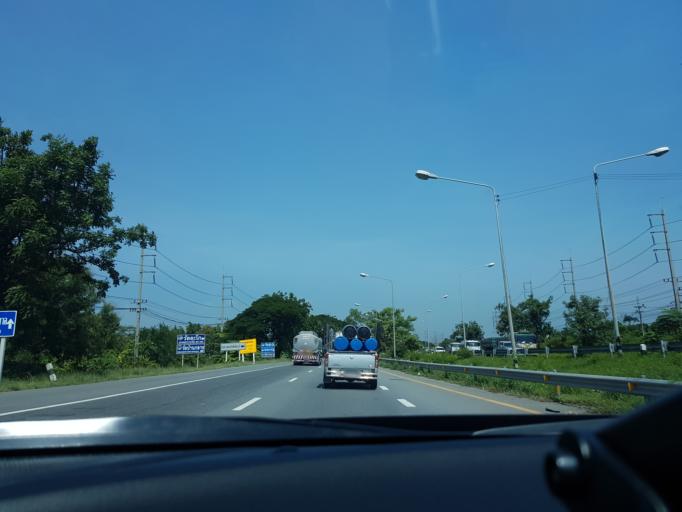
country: TH
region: Sara Buri
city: Saraburi
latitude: 14.5325
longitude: 100.8859
